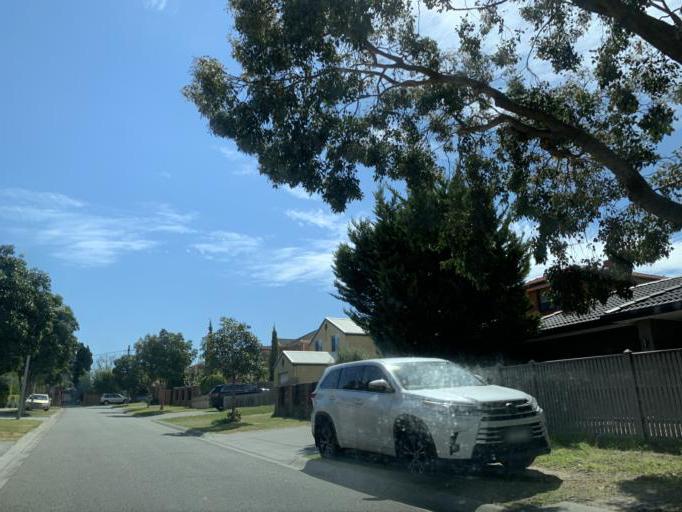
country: AU
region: Victoria
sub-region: Bayside
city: Hampton East
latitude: -37.9389
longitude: 145.0279
